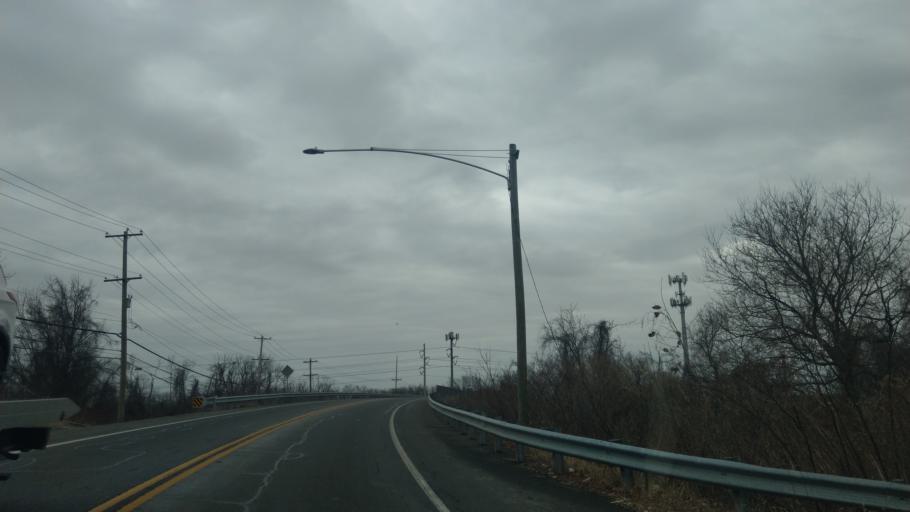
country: US
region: Pennsylvania
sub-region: Bucks County
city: Bristol
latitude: 40.1266
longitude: -74.8656
